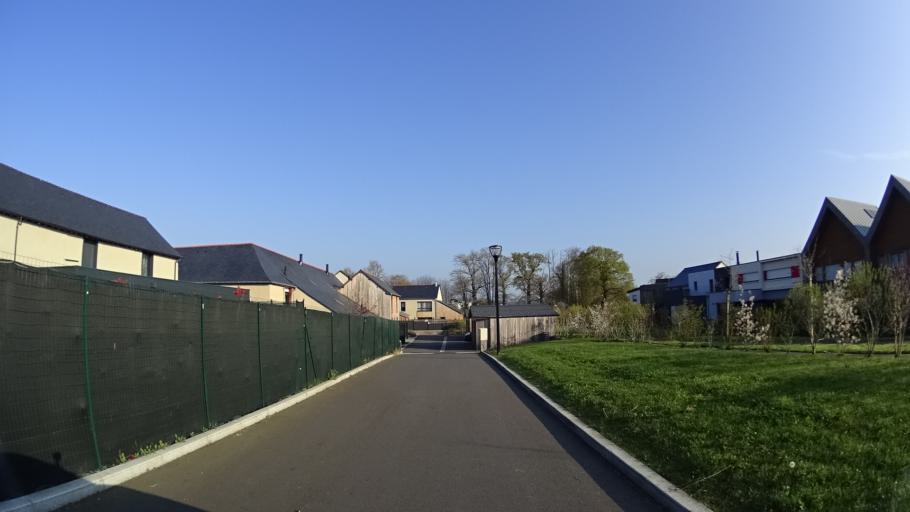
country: FR
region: Brittany
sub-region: Departement d'Ille-et-Vilaine
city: Pace
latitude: 48.1562
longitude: -1.7600
